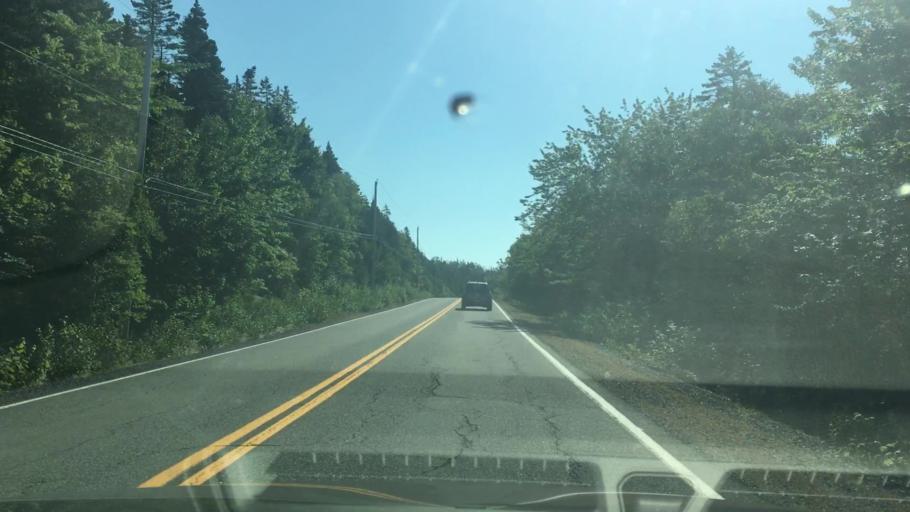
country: CA
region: Nova Scotia
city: Cole Harbour
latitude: 44.8128
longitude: -62.8402
